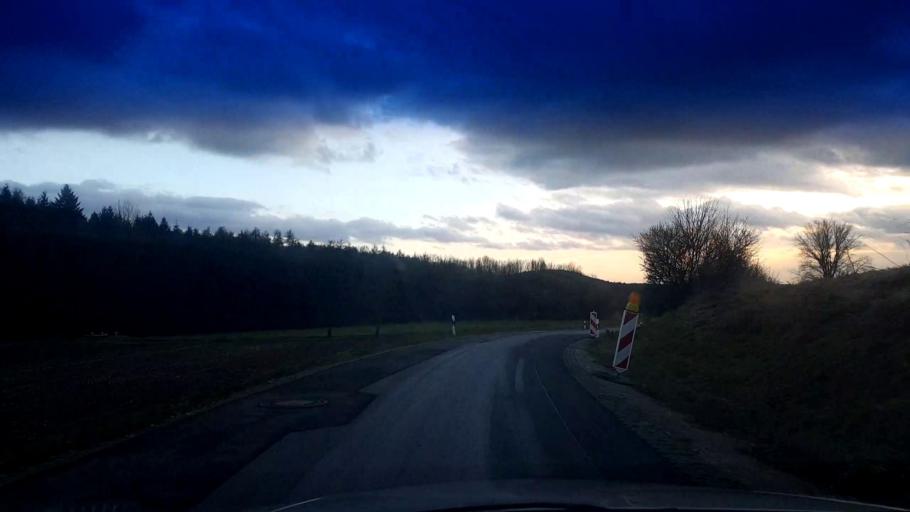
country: DE
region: Bavaria
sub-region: Upper Franconia
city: Buttenheim
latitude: 49.8271
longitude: 11.0571
